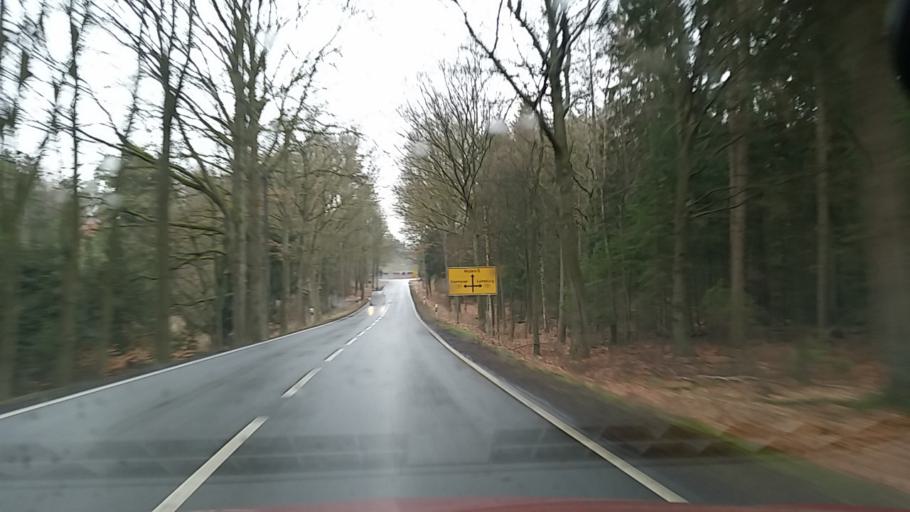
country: DE
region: Lower Saxony
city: Unterluss
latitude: 52.7899
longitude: 10.3872
